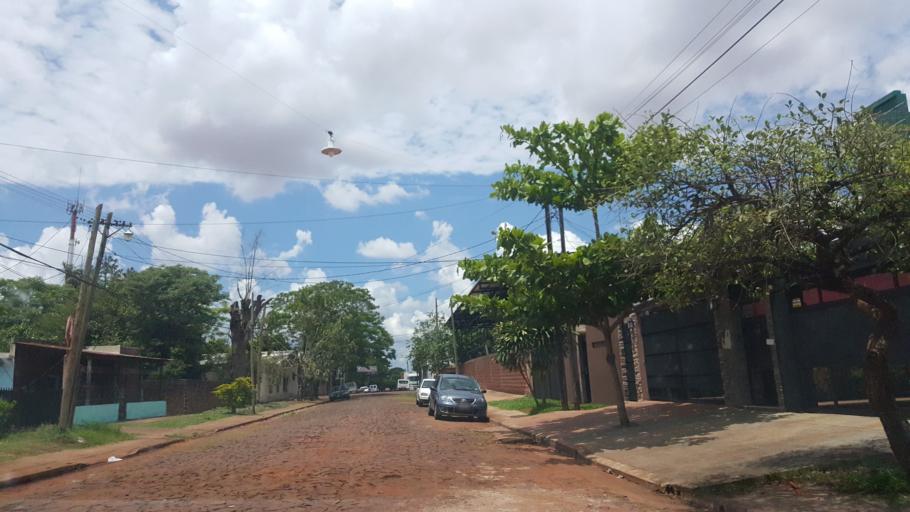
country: AR
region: Misiones
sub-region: Departamento de Capital
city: Posadas
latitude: -27.3778
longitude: -55.9132
